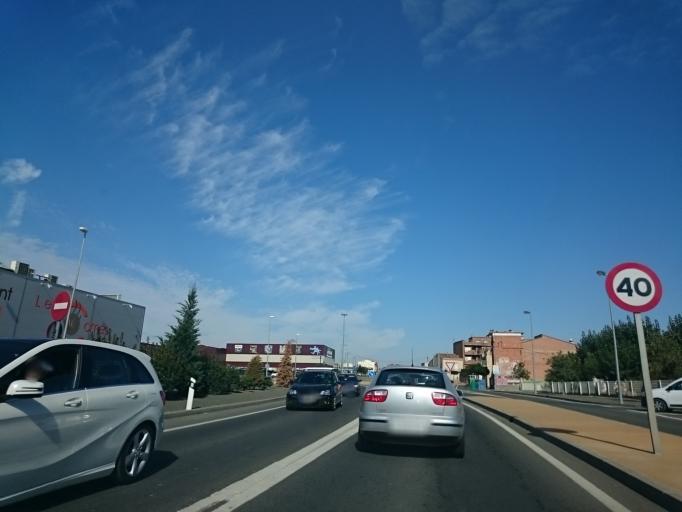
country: ES
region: Catalonia
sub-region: Provincia de Lleida
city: Torrefarrera
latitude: 41.6687
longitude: 0.6065
